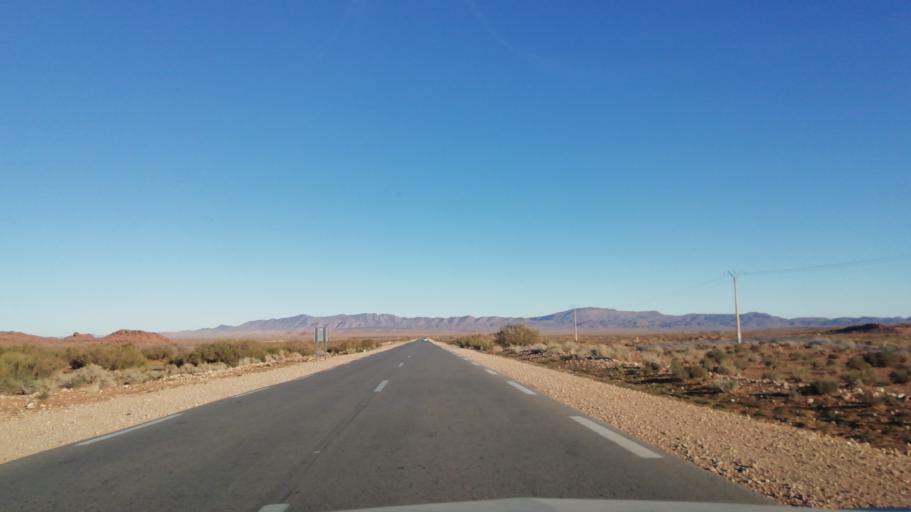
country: DZ
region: El Bayadh
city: El Abiodh Sidi Cheikh
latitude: 33.1701
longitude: 0.4998
